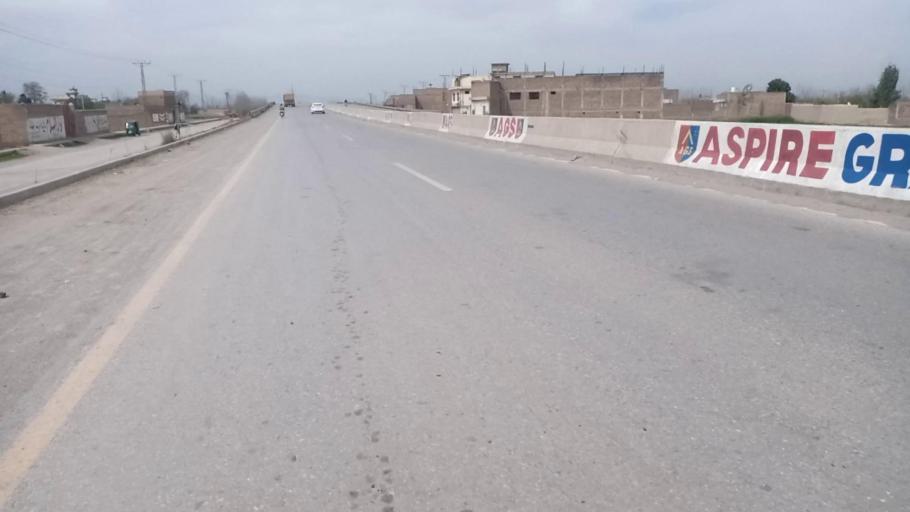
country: PK
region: Khyber Pakhtunkhwa
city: Peshawar
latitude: 34.0471
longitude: 71.6154
